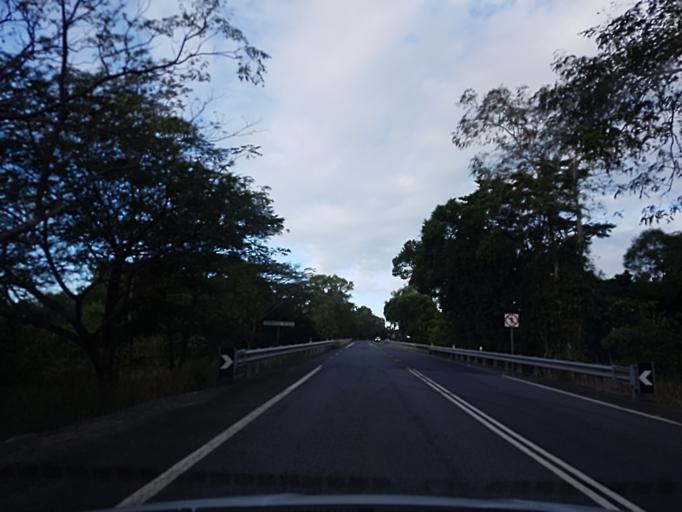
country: AU
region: Queensland
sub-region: Cairns
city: Port Douglas
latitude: -16.5531
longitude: 145.4808
